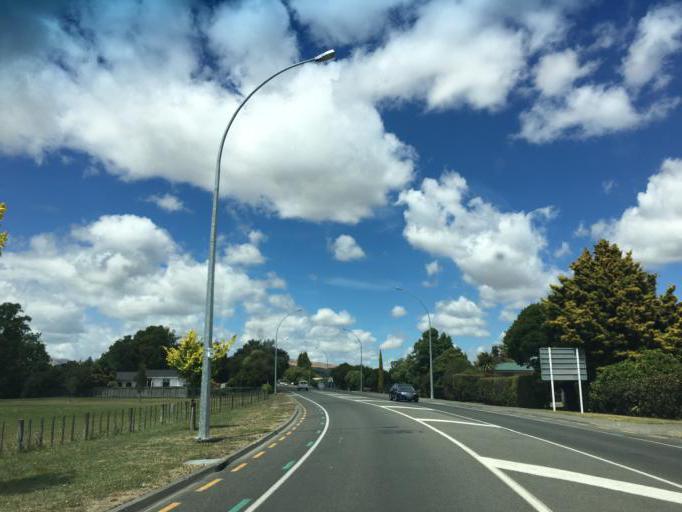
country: NZ
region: Hawke's Bay
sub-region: Hastings District
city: Hastings
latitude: -39.6597
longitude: 176.8853
